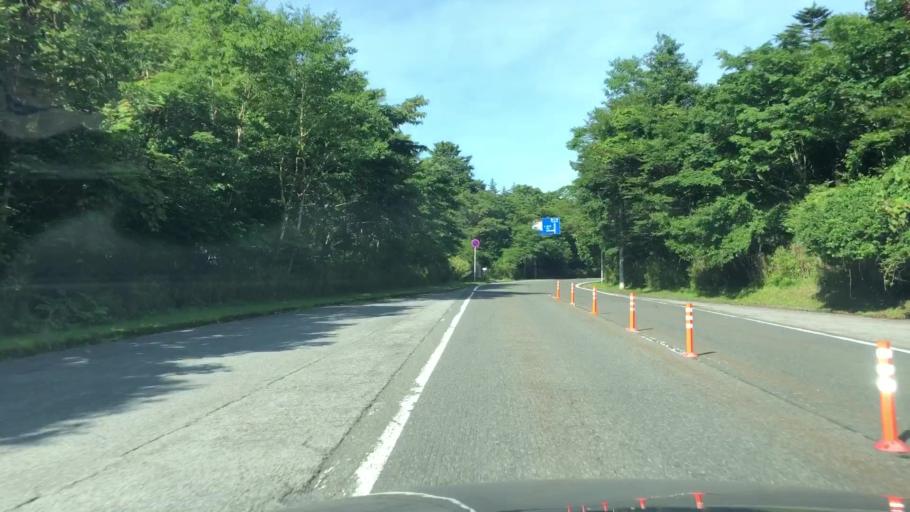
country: JP
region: Shizuoka
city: Gotemba
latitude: 35.3071
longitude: 138.7740
